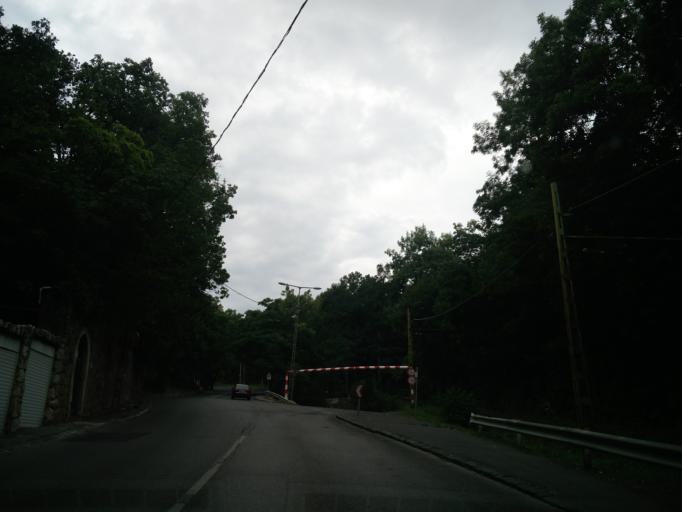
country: HU
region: Budapest
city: Budapest XII. keruelet
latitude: 47.5021
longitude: 18.9893
